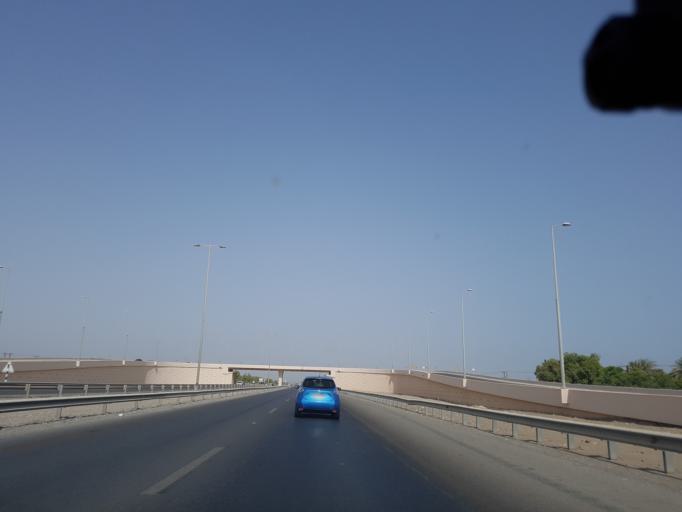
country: OM
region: Al Batinah
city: Barka'
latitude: 23.7277
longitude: 57.7164
